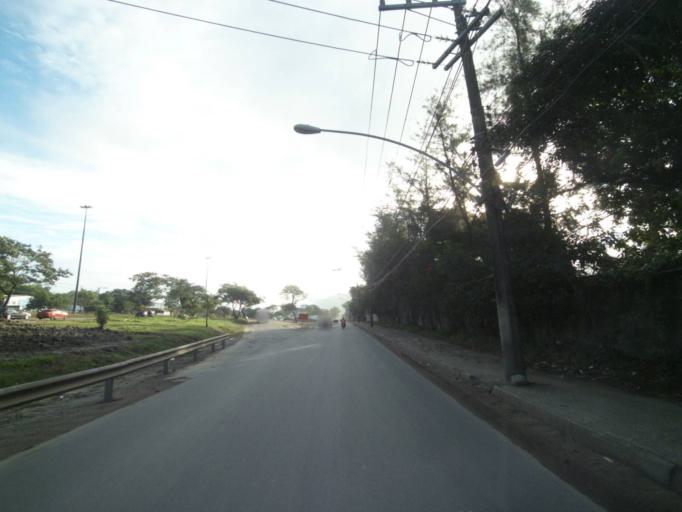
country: BR
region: Rio de Janeiro
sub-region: Nilopolis
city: Nilopolis
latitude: -22.8564
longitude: -43.4746
